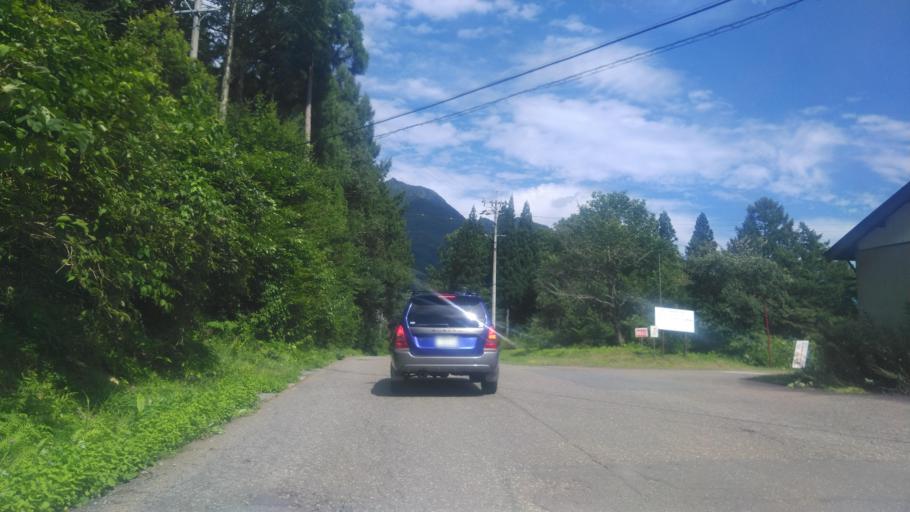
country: JP
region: Niigata
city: Arai
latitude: 36.8382
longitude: 138.1684
